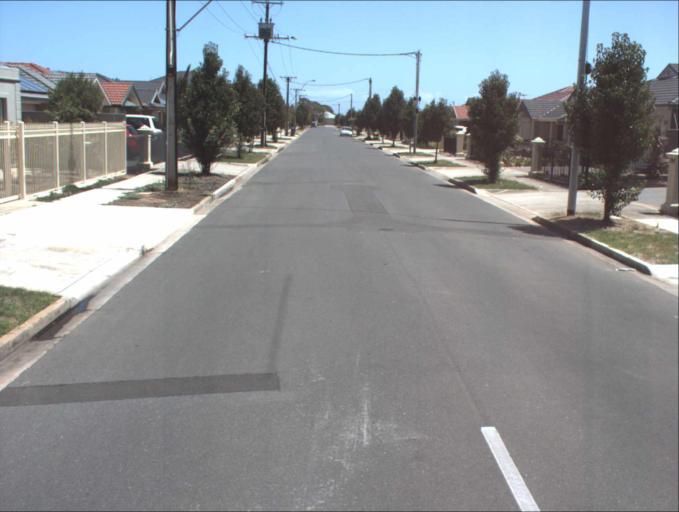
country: AU
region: South Australia
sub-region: Charles Sturt
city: Woodville North
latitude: -34.8621
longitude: 138.5563
